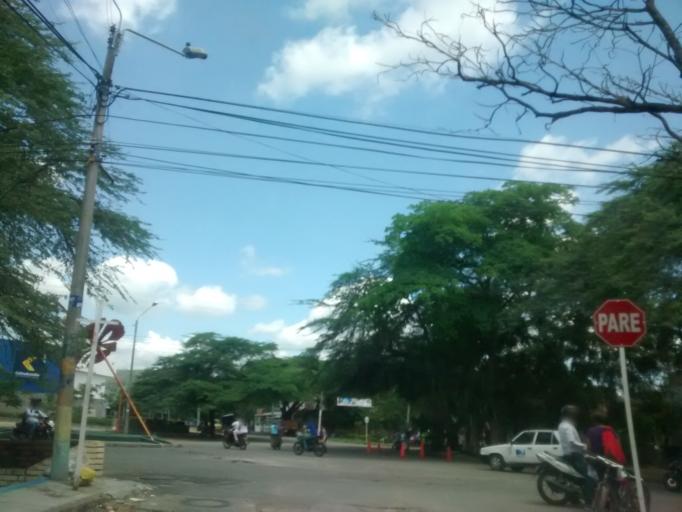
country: CO
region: Cundinamarca
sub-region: Girardot
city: Girardot City
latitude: 4.3103
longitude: -74.7911
